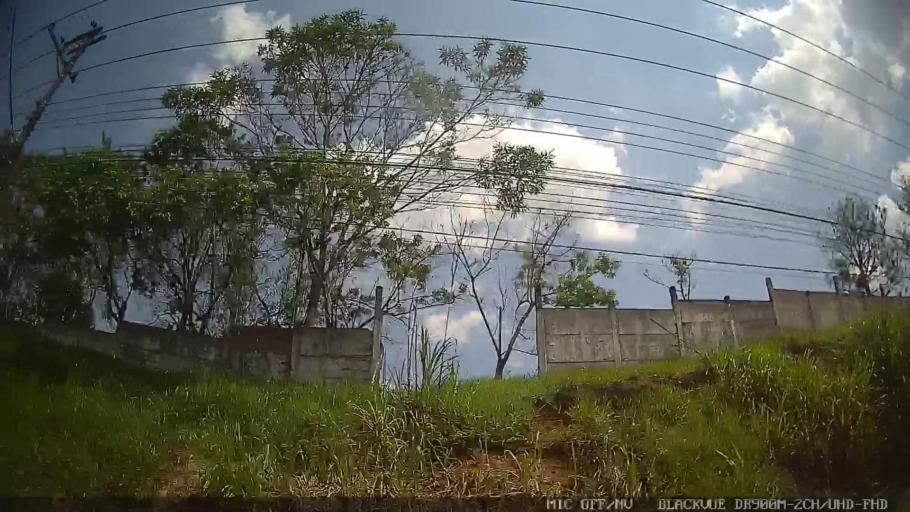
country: BR
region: Sao Paulo
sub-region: Itapecerica Da Serra
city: Itapecerica da Serra
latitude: -23.6899
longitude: -46.8157
